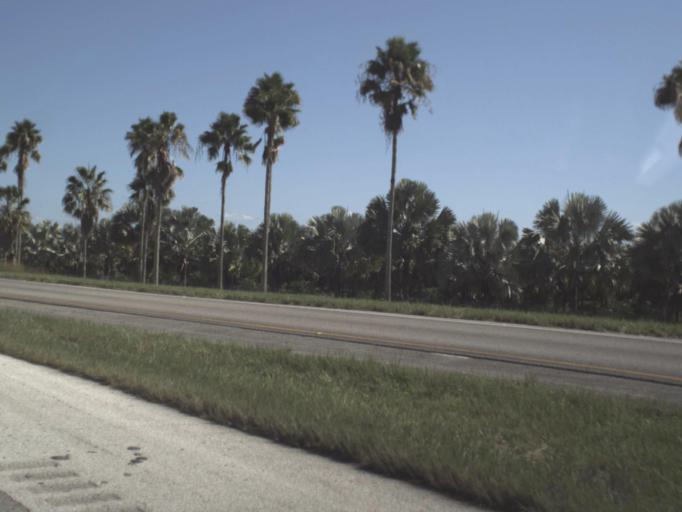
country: US
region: Florida
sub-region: Miami-Dade County
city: Goulds
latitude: 25.5343
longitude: -80.3685
